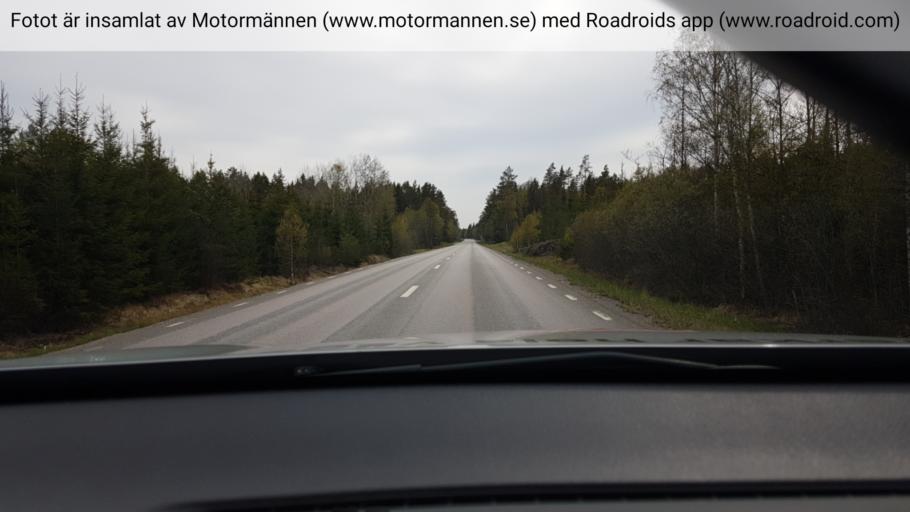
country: SE
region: Stockholm
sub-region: Norrtalje Kommun
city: Nykvarn
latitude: 59.9021
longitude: 18.0930
